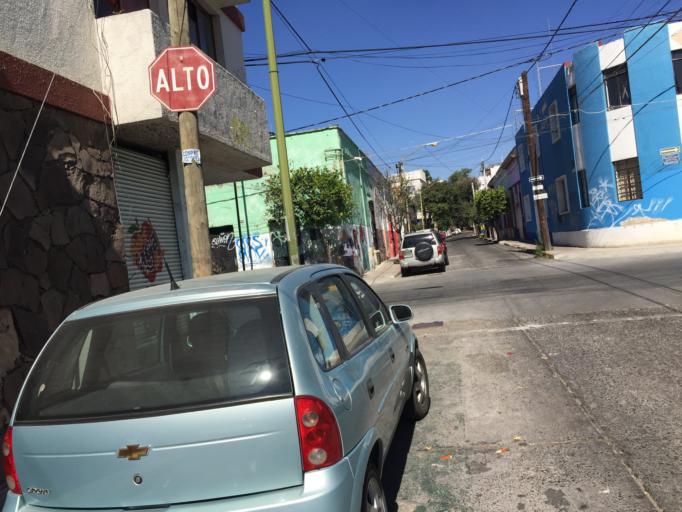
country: MX
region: Jalisco
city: Guadalajara
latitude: 20.6726
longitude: -103.3558
